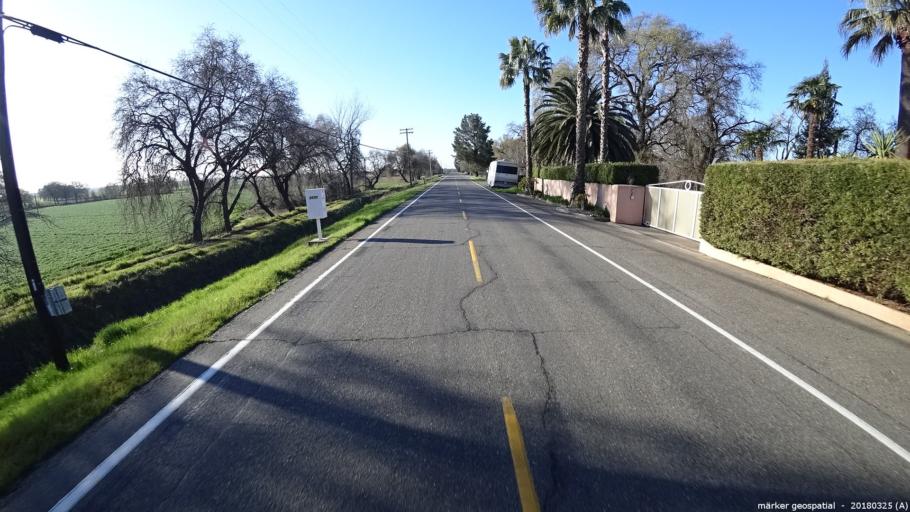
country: US
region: California
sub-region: Yolo County
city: West Sacramento
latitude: 38.6327
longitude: -121.5610
